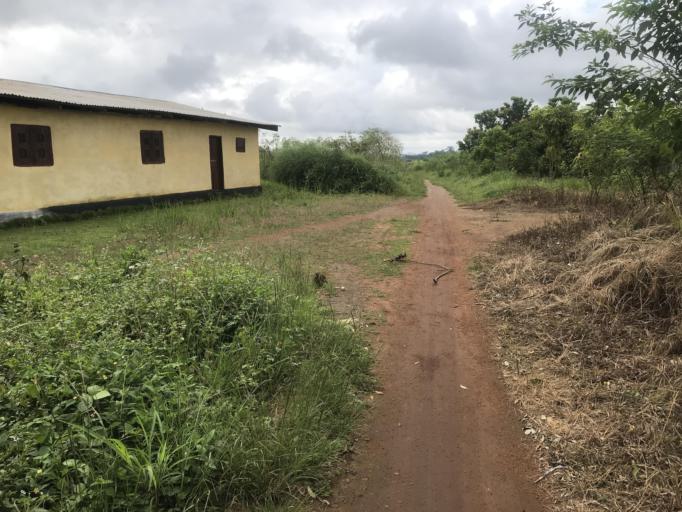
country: SL
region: Eastern Province
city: Buedu
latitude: 8.4652
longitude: -10.3155
